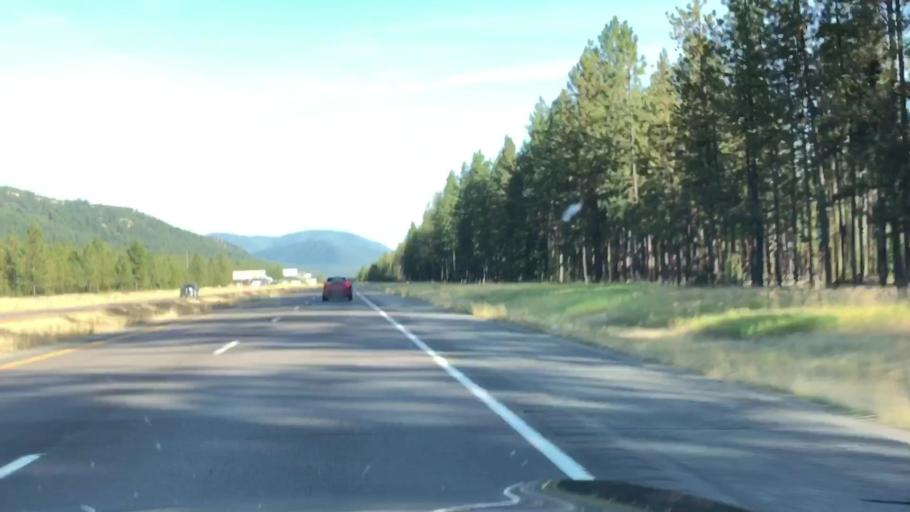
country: US
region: Montana
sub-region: Mineral County
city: Superior
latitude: 47.1609
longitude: -114.8450
